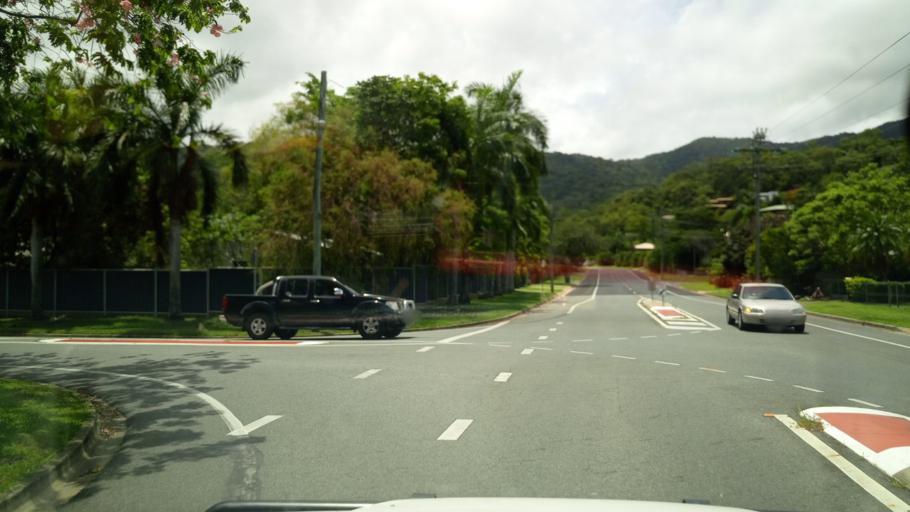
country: AU
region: Queensland
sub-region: Cairns
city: Yorkeys Knob
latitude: -16.8315
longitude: 145.6912
